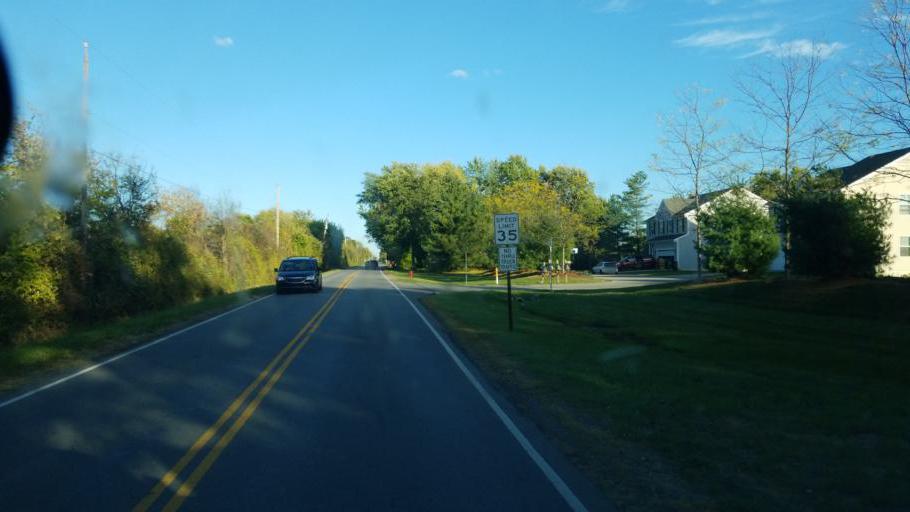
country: US
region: Ohio
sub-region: Franklin County
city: New Albany
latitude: 40.0182
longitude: -82.7700
